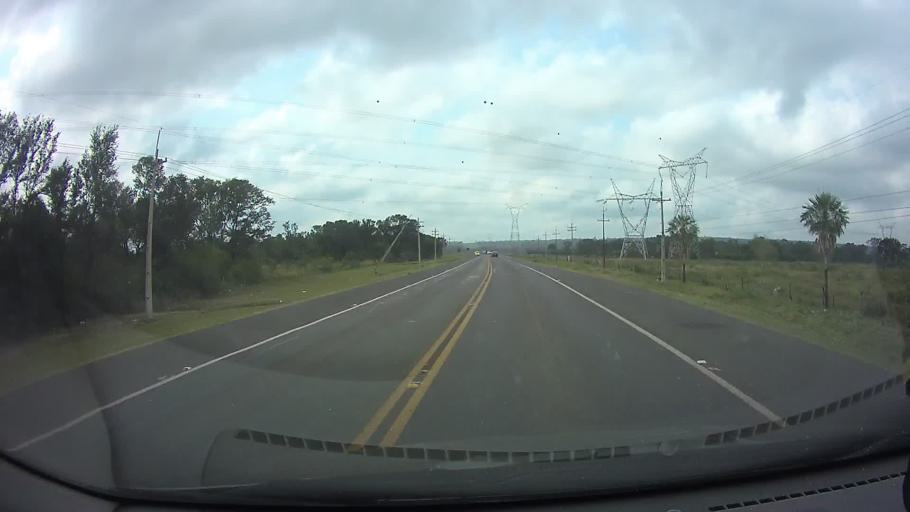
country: PY
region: Central
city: Limpio
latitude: -25.1145
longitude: -57.4239
